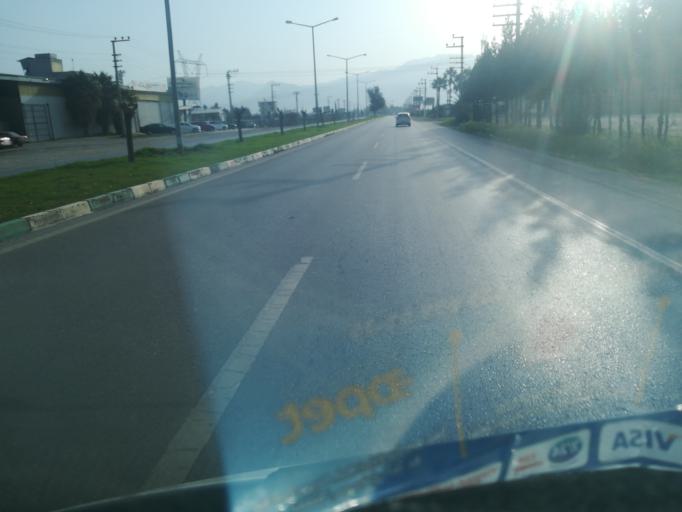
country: TR
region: Osmaniye
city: Toprakkale
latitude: 37.0561
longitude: 36.1946
